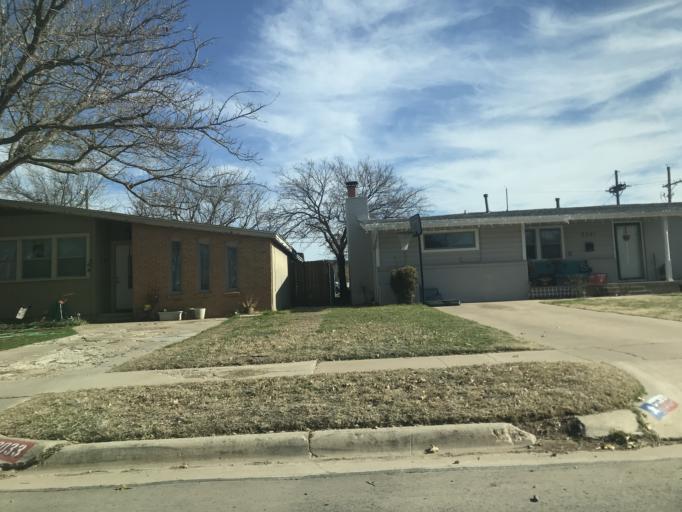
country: US
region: Texas
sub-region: Taylor County
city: Abilene
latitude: 32.4240
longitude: -99.7584
